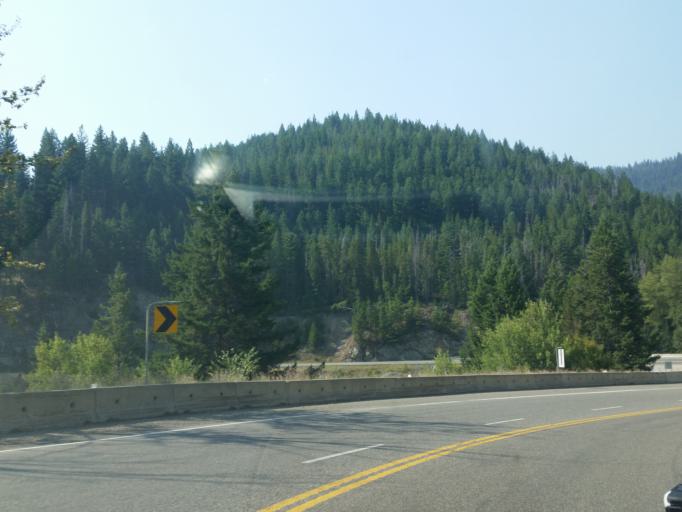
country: CA
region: British Columbia
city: Princeton
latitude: 49.1901
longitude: -120.5598
